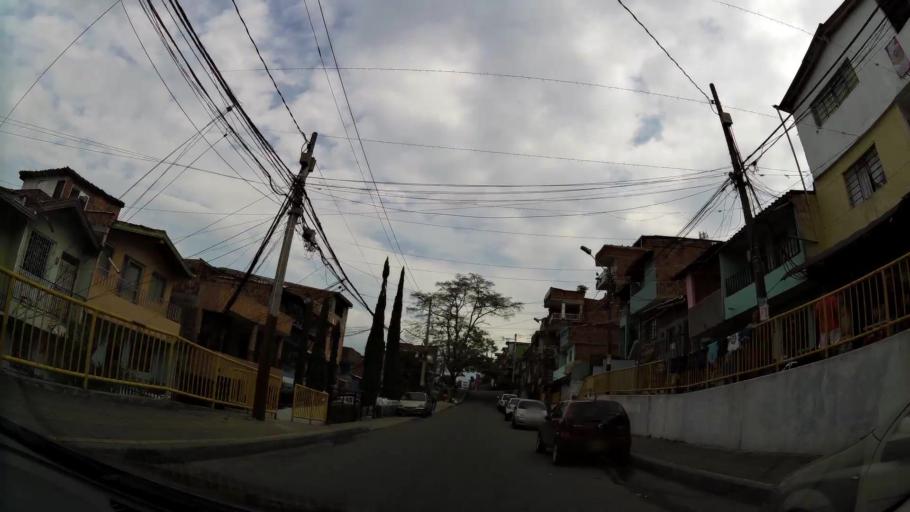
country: CO
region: Antioquia
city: Medellin
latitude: 6.2823
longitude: -75.5520
